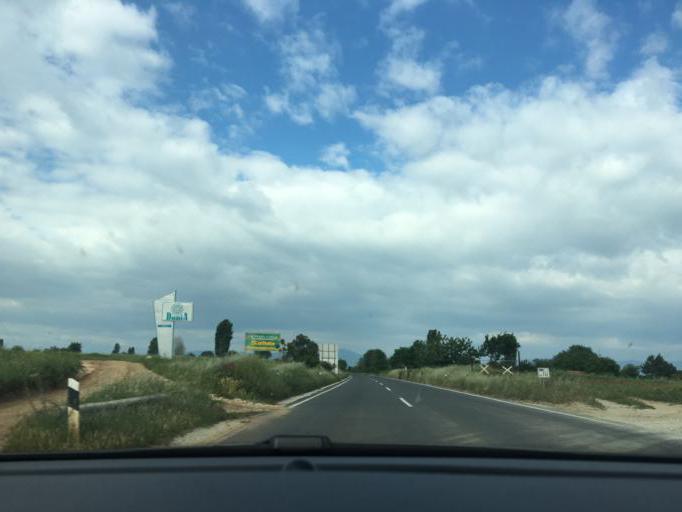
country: MK
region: Prilep
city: Prilep
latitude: 41.3257
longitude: 21.5418
